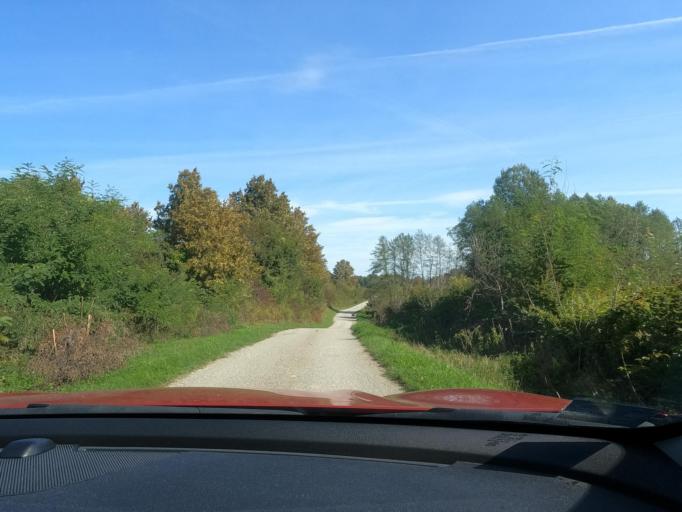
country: HR
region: Sisacko-Moslavacka
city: Petrinja
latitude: 45.3400
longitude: 16.2294
